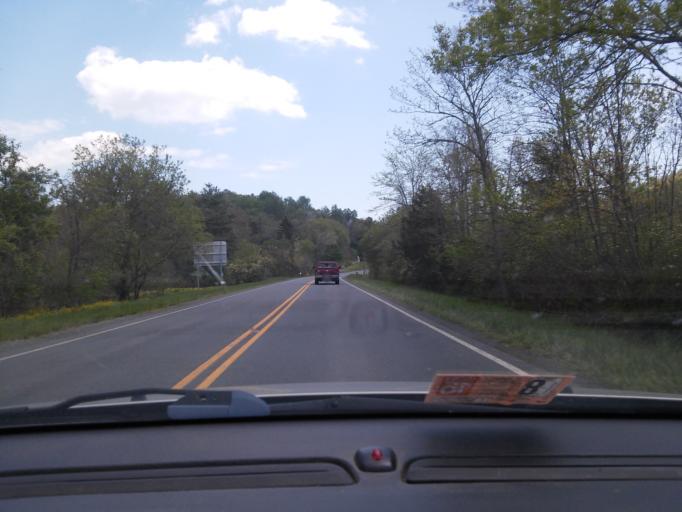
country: US
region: Virginia
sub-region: Warren County
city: Front Royal
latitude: 38.8768
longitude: -78.1483
